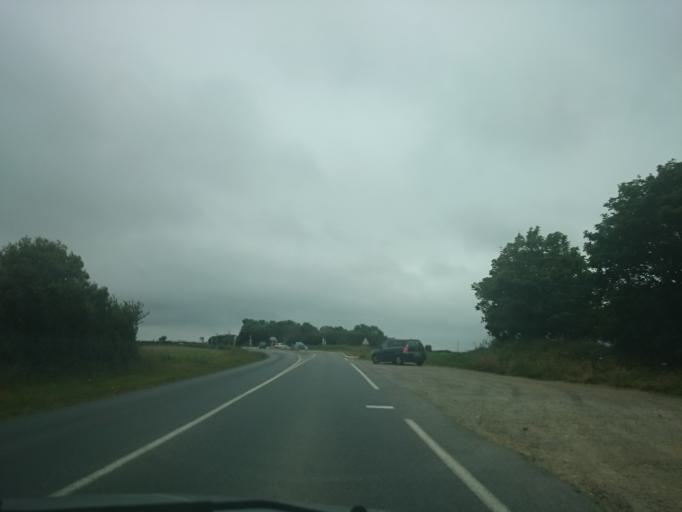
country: FR
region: Brittany
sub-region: Departement du Finistere
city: Saint-Pabu
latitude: 48.5509
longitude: -4.6159
